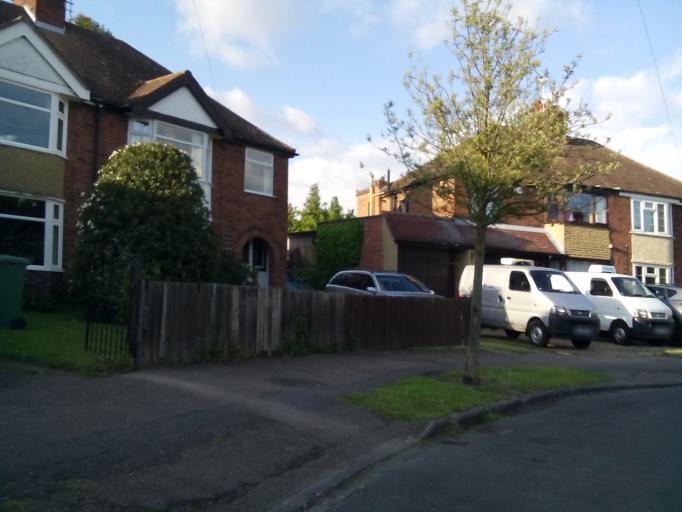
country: GB
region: England
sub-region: Cambridgeshire
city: Cambridge
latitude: 52.1900
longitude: 0.1481
